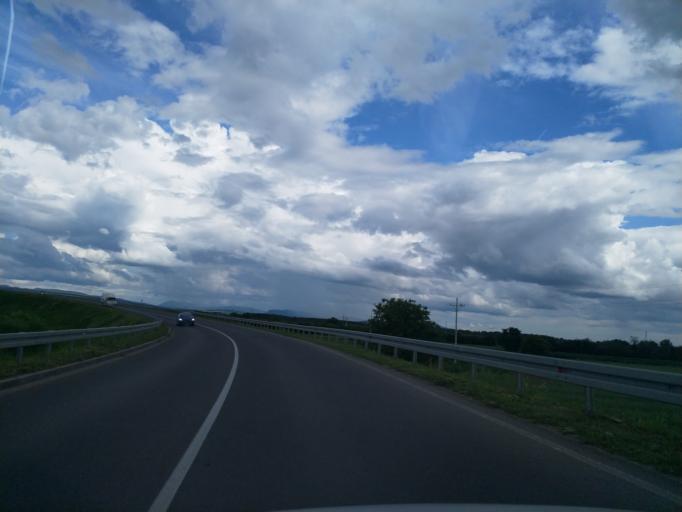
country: RS
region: Central Serbia
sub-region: Pomoravski Okrug
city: Cuprija
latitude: 43.9479
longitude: 21.3263
